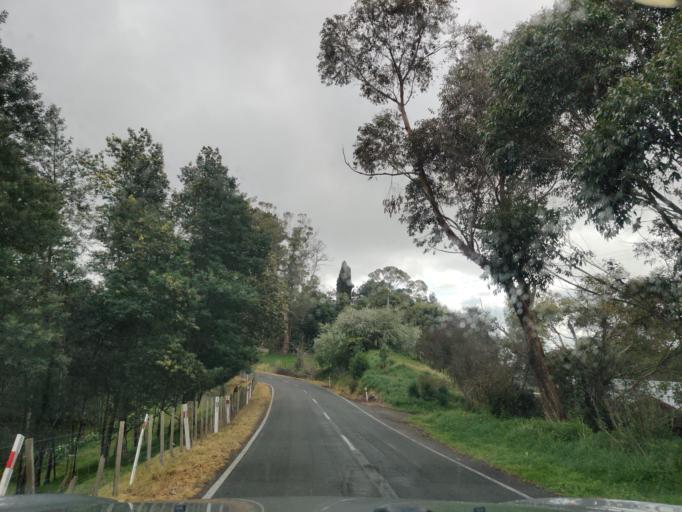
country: NZ
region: Hawke's Bay
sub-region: Hastings District
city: Hastings
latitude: -39.6794
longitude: 176.8964
